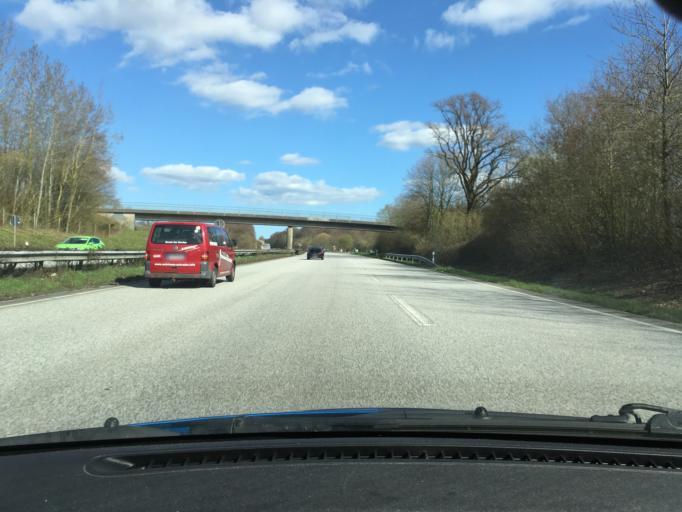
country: DE
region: Schleswig-Holstein
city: Krummwisch
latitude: 54.3140
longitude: 9.9083
